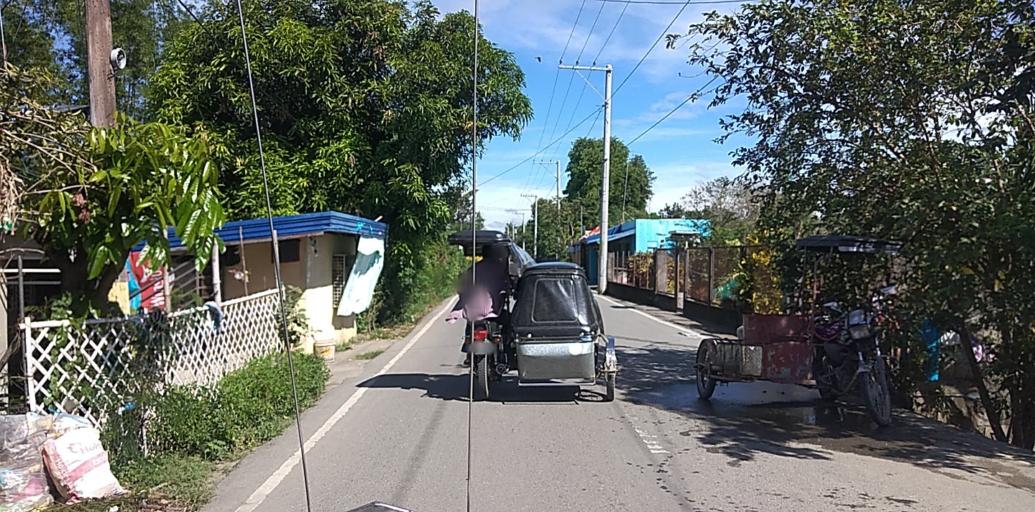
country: PH
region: Central Luzon
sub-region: Province of Pampanga
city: Candaba
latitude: 15.0881
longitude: 120.8109
